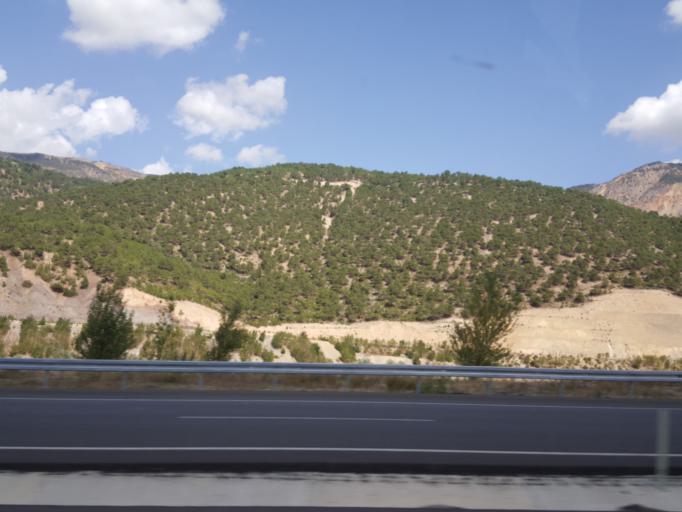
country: TR
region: Sivas
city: Dogansar
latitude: 40.3175
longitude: 37.6310
